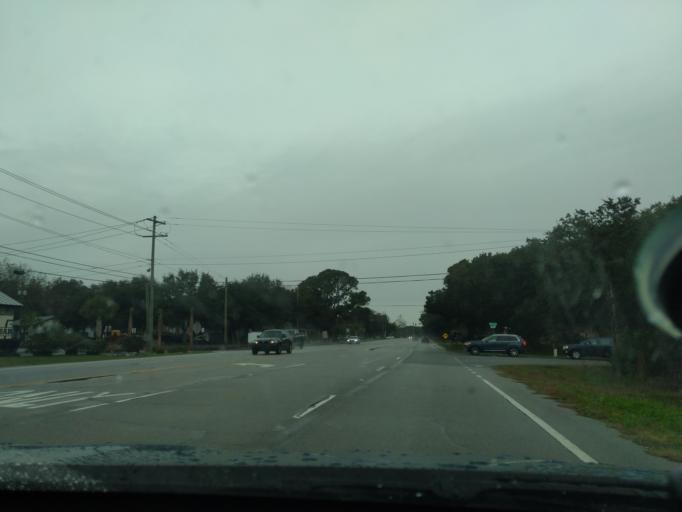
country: US
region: South Carolina
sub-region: Charleston County
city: Folly Beach
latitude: 32.6915
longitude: -79.9638
